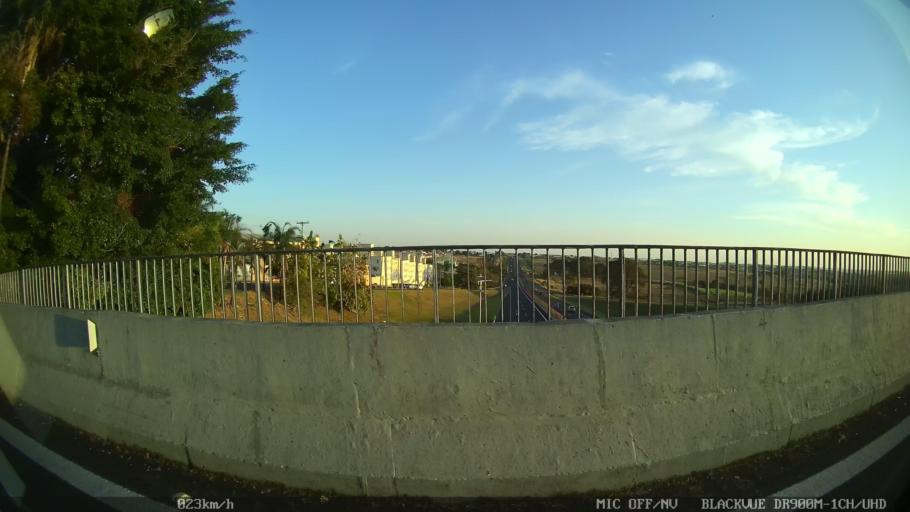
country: BR
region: Sao Paulo
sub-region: Franca
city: Franca
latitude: -20.5147
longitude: -47.4152
